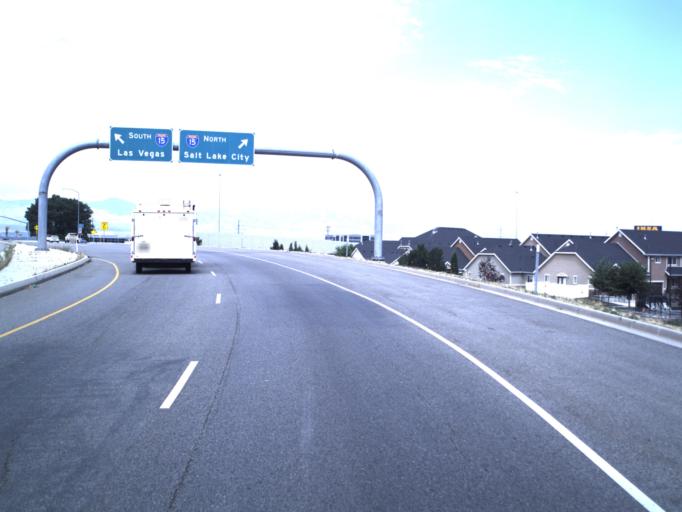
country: US
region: Utah
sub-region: Salt Lake County
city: Draper
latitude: 40.5042
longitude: -111.8872
